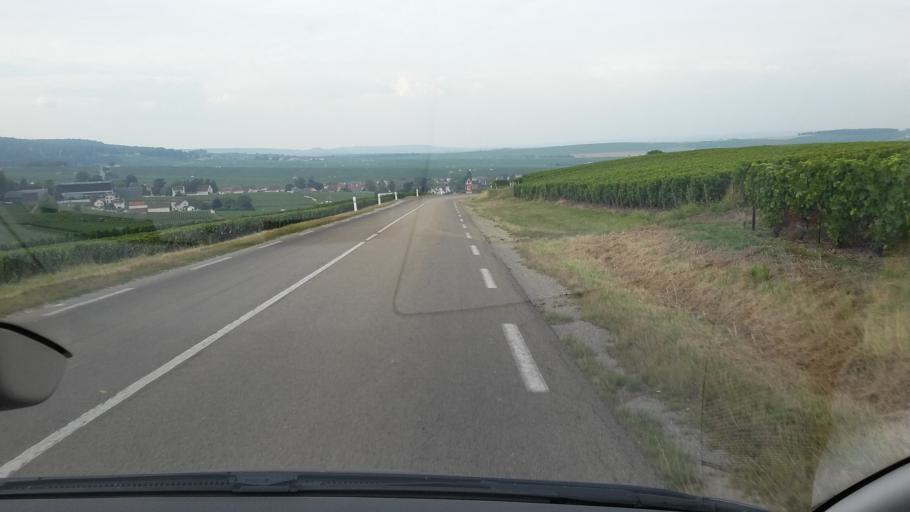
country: FR
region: Champagne-Ardenne
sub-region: Departement de la Marne
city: Rilly-la-Montagne
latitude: 49.1535
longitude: 4.0939
